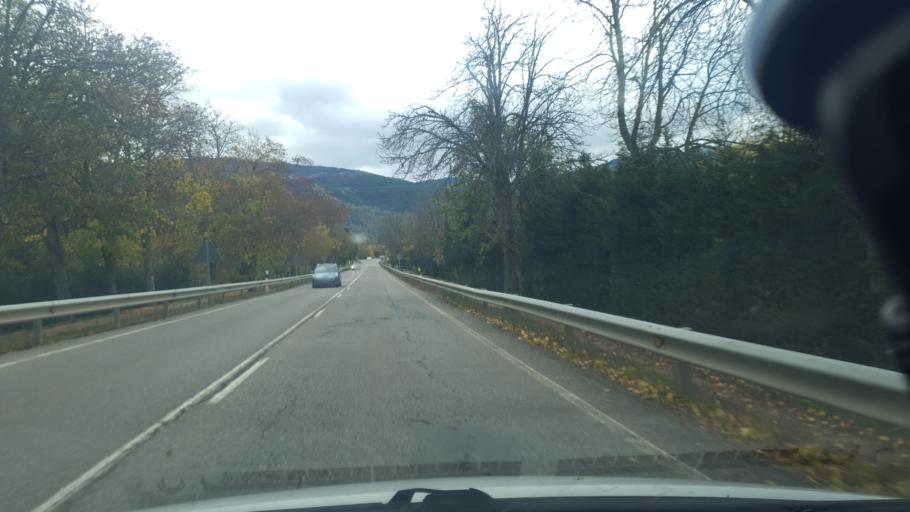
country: ES
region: Castille and Leon
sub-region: Provincia de Segovia
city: San Ildefonso
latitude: 40.9042
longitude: -4.0196
